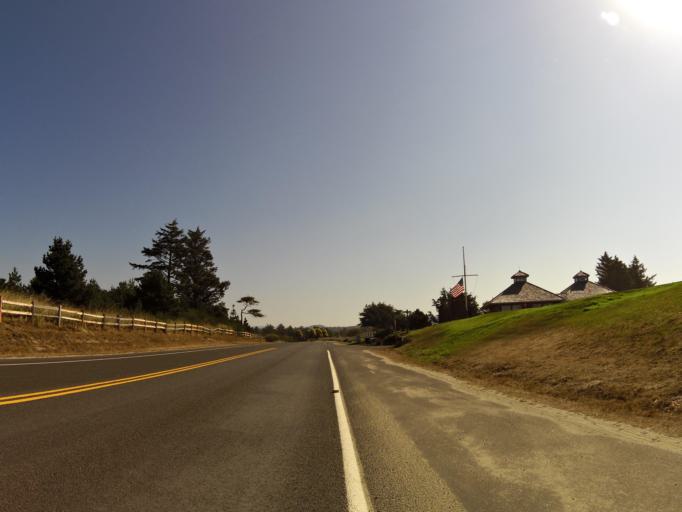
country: US
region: Oregon
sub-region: Clatsop County
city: Gearhart
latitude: 46.0485
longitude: -123.9253
